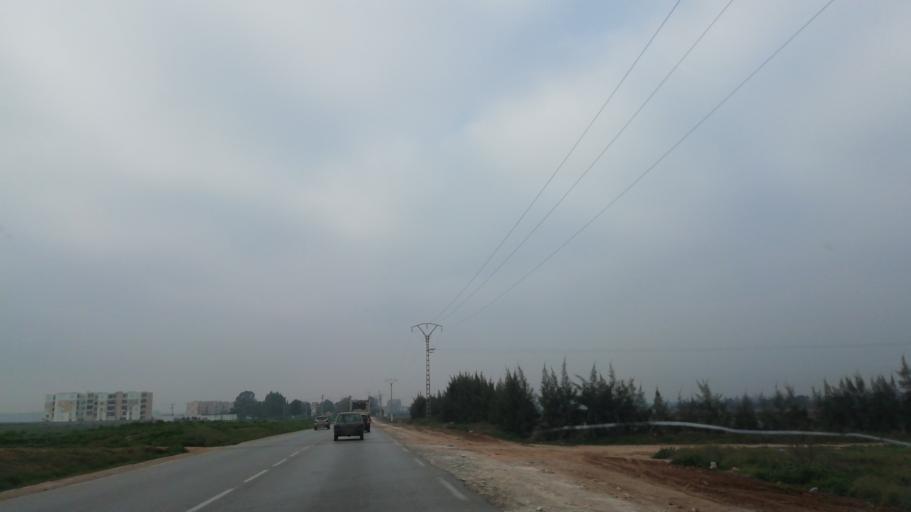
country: DZ
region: Relizane
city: Djidiouia
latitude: 35.9152
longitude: 0.7862
